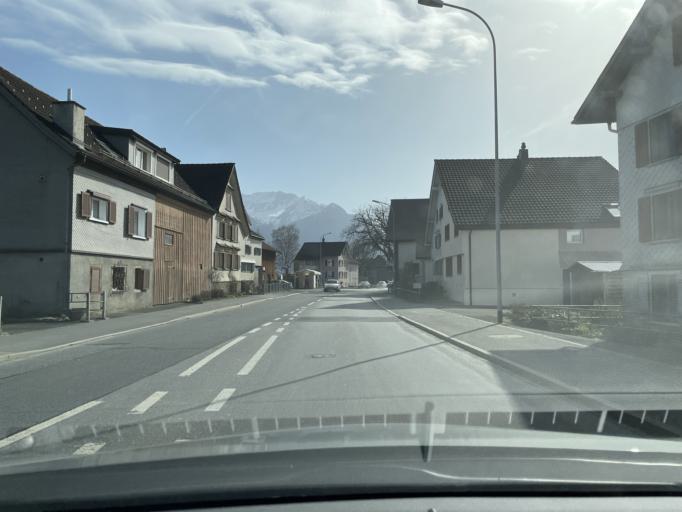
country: CH
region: Saint Gallen
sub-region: Wahlkreis Werdenberg
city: Buchs
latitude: 47.1463
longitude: 9.4847
